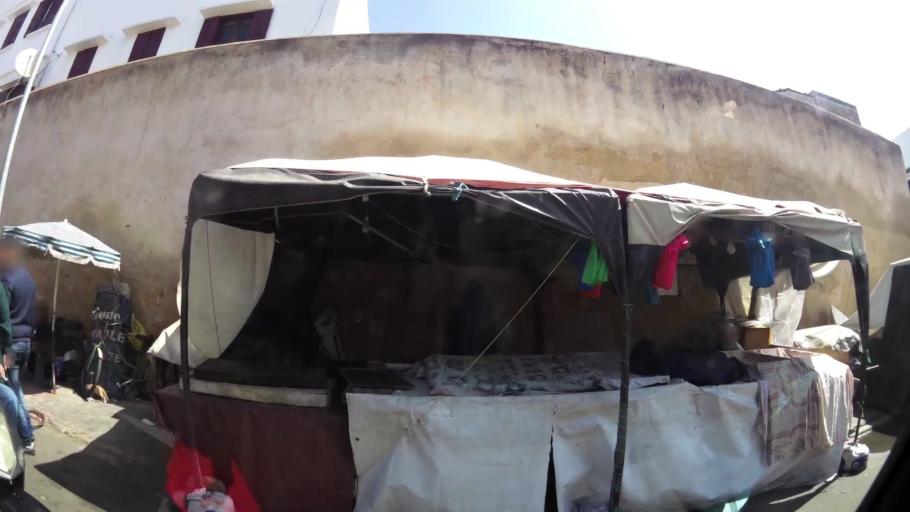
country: MA
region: Grand Casablanca
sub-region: Casablanca
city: Casablanca
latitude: 33.5974
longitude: -7.6210
